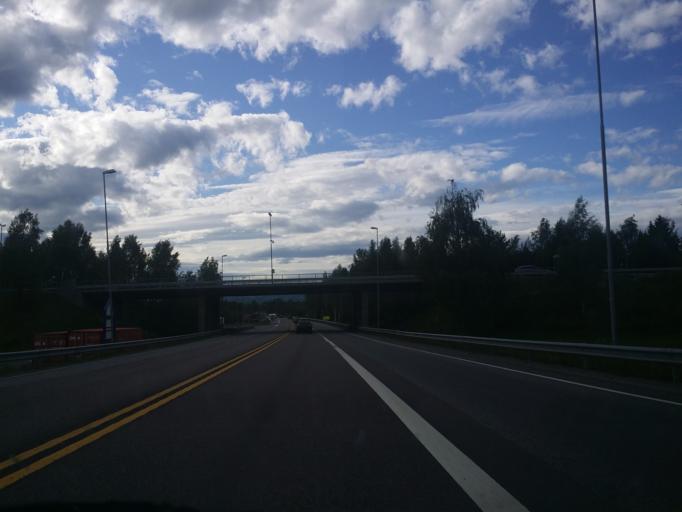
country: NO
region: Hedmark
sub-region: Hamar
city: Hamar
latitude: 60.7995
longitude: 11.1182
